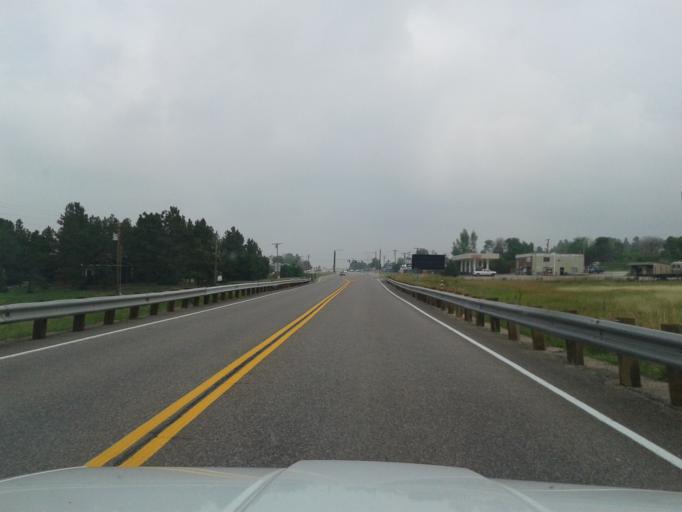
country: US
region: Colorado
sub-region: Douglas County
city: The Pinery
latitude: 39.3878
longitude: -104.7522
